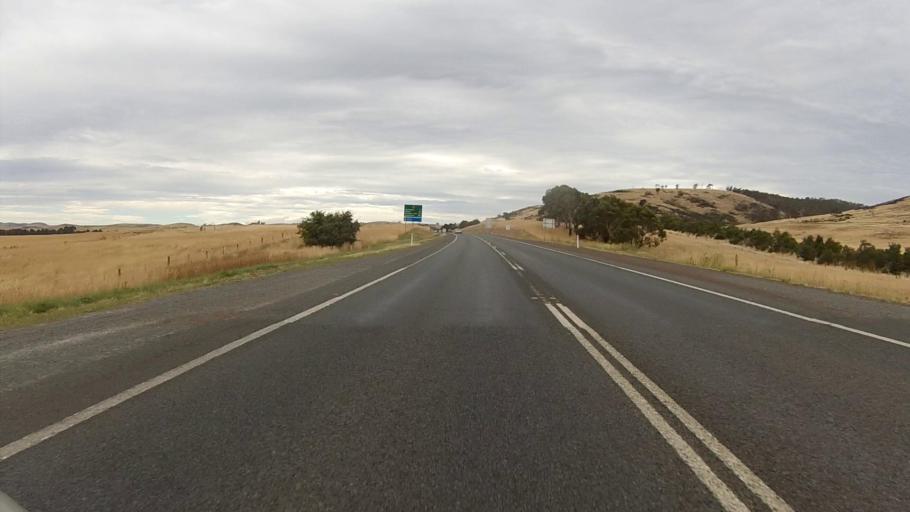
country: AU
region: Tasmania
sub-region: Brighton
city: Bridgewater
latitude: -42.3832
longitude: 147.3161
